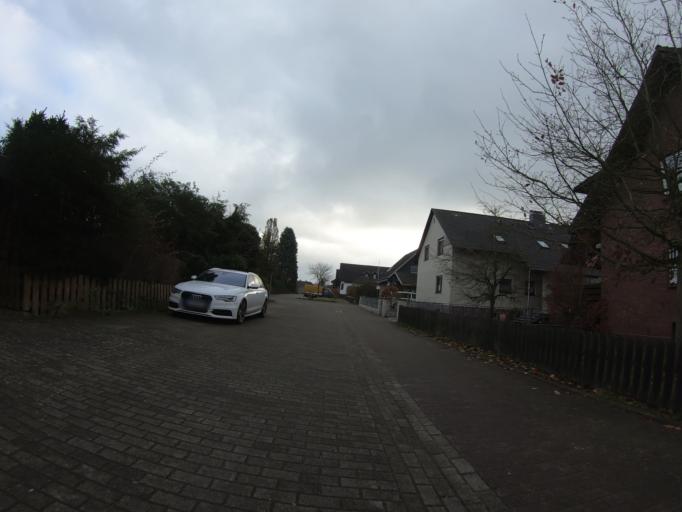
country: DE
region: Lower Saxony
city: Wagenhoff
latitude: 52.5539
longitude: 10.5232
